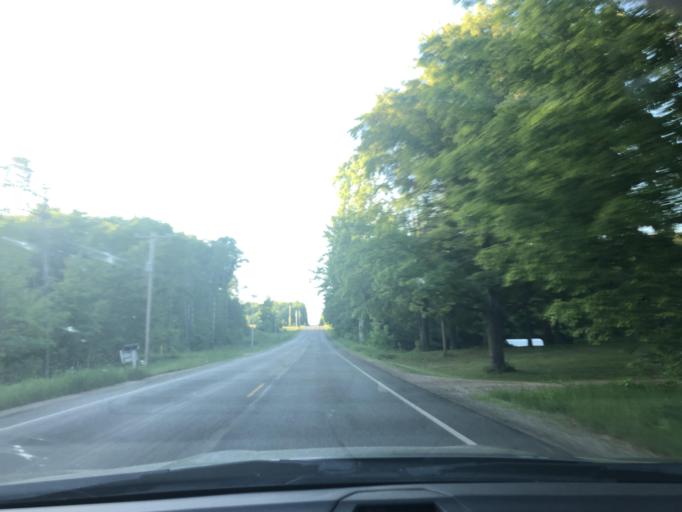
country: US
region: Michigan
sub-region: Missaukee County
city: Lake City
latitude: 44.4624
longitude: -85.0743
